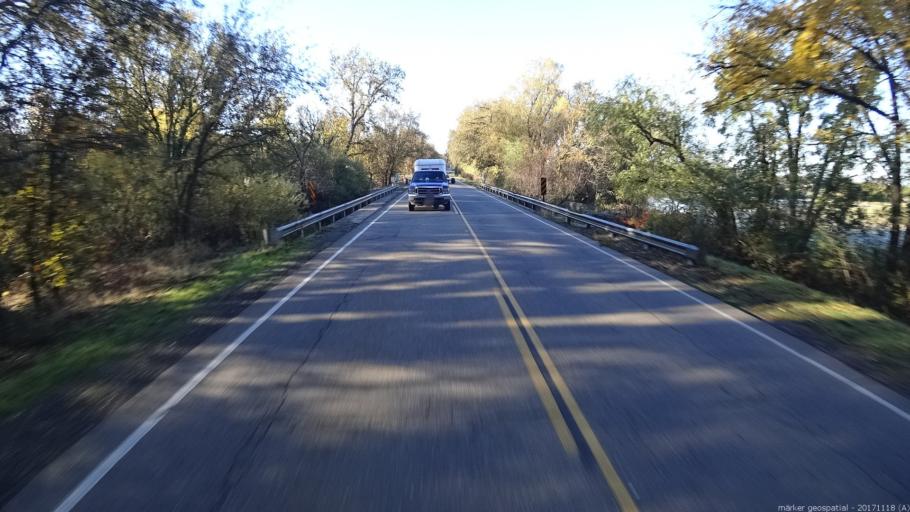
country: US
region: California
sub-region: Shasta County
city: Anderson
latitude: 40.4441
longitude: -122.2620
